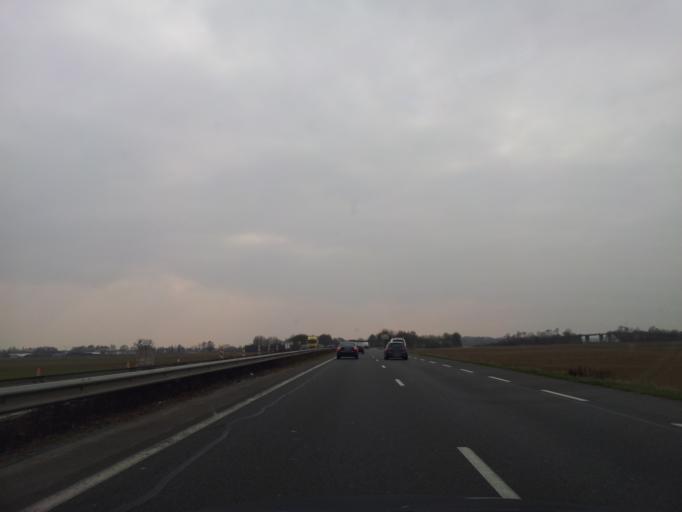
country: FR
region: Alsace
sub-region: Departement du Bas-Rhin
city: Lipsheim
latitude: 48.4825
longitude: 7.6721
